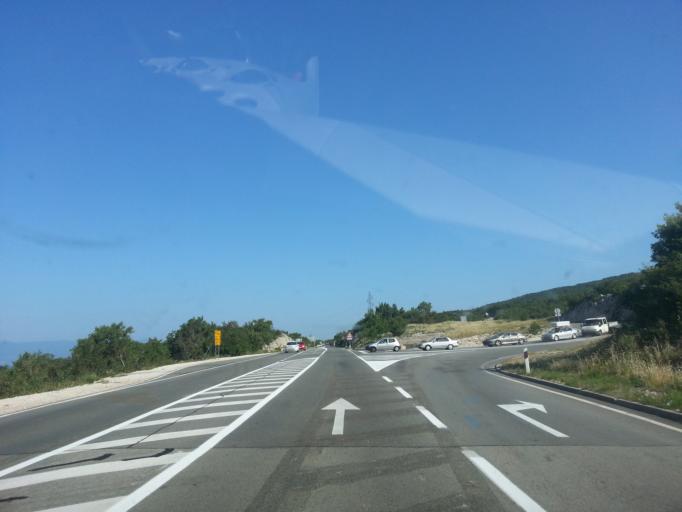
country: HR
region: Primorsko-Goranska
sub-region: Grad Crikvenica
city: Jadranovo
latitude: 45.2362
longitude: 14.6202
